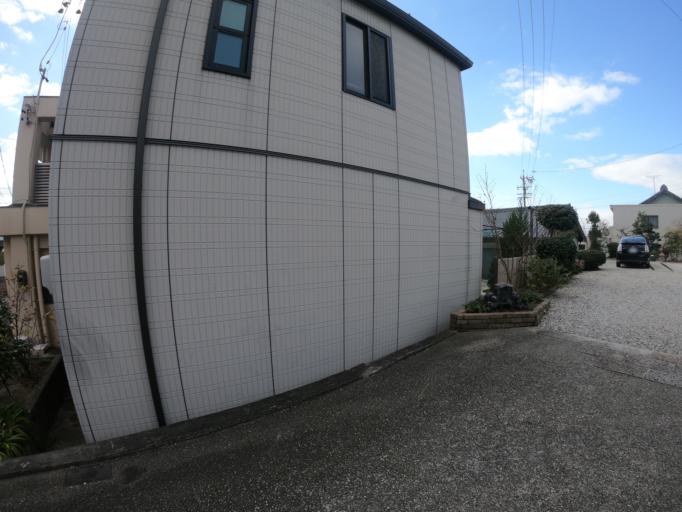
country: JP
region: Aichi
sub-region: Toyota-shi
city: Toyota
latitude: 35.1218
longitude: 137.0453
